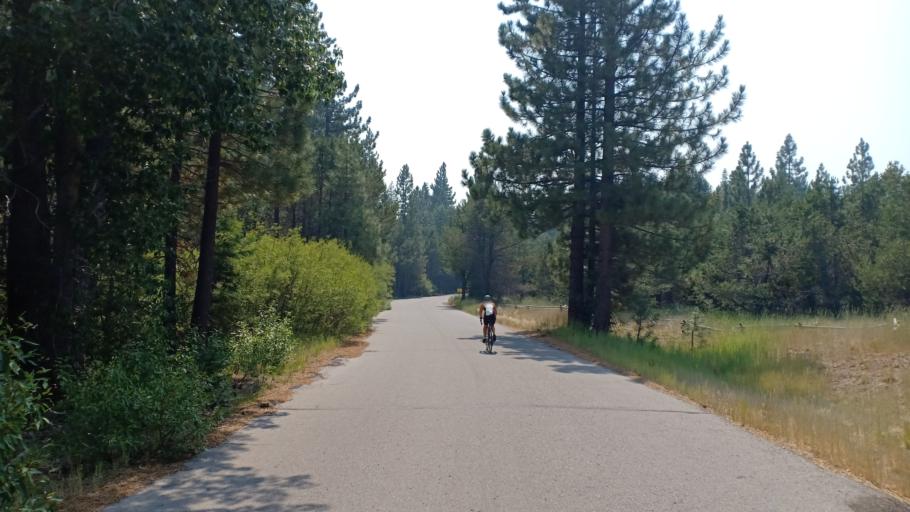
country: US
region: California
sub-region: Placer County
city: Sunnyside-Tahoe City
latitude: 39.1076
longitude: -120.1951
